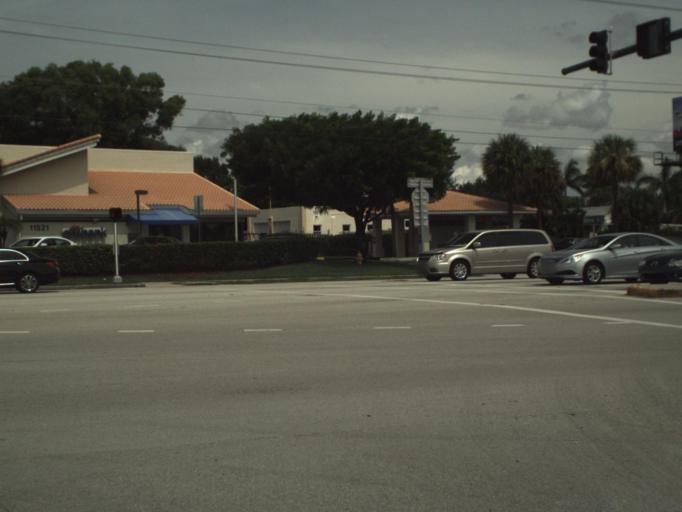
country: US
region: Florida
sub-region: Palm Beach County
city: North Palm Beach
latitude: 26.8442
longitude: -80.0610
